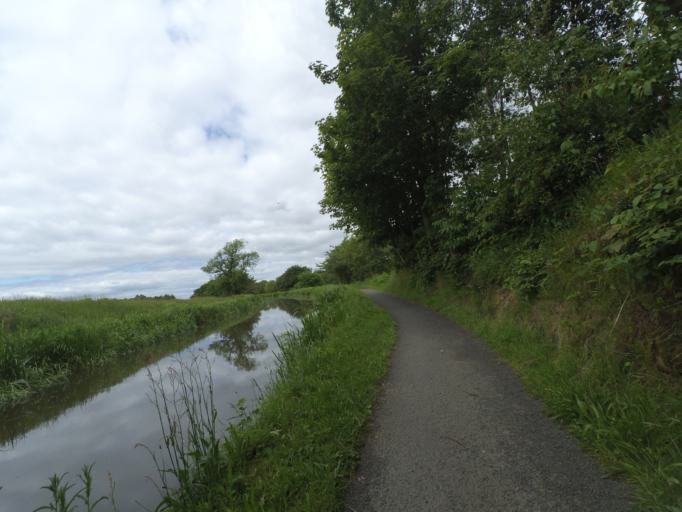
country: GB
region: Scotland
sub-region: Falkirk
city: Polmont
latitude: 55.9753
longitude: -3.6759
